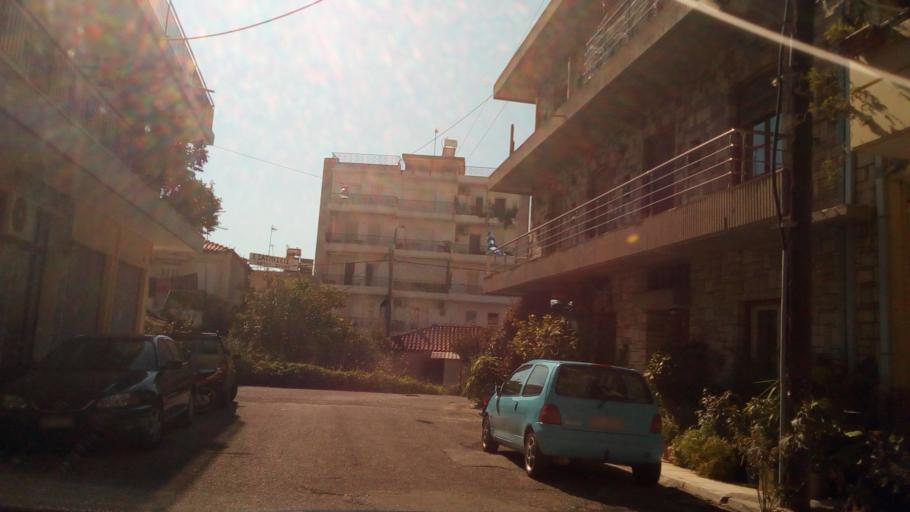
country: GR
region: West Greece
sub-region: Nomos Aitolias kai Akarnanias
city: Nafpaktos
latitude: 38.3929
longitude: 21.8406
